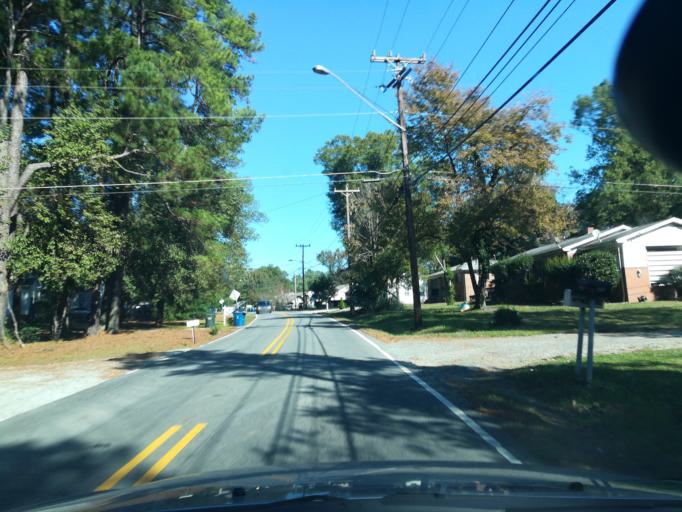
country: US
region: North Carolina
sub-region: Durham County
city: Durham
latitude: 36.0371
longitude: -78.9085
